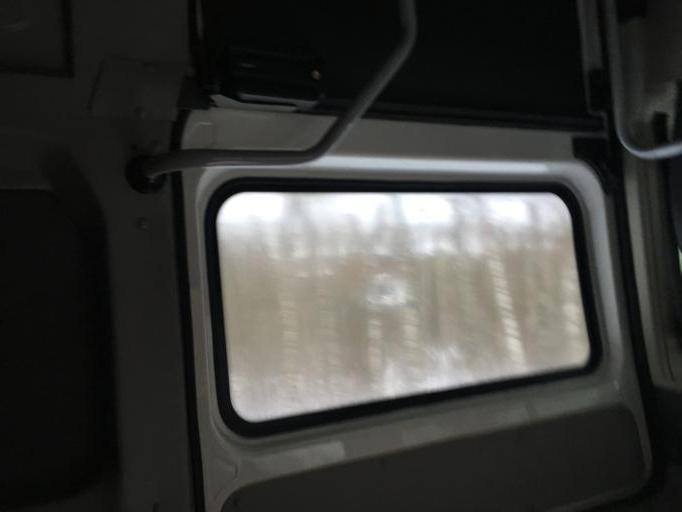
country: RU
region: Tula
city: Krapivna
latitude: 54.1374
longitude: 37.2767
